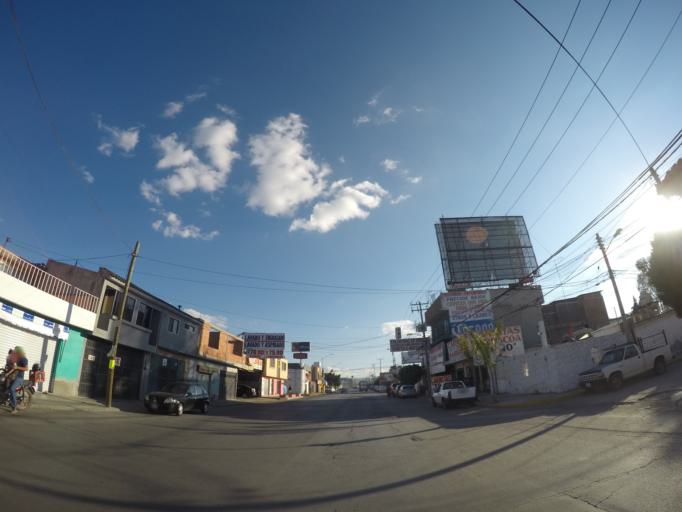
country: MX
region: San Luis Potosi
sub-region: San Luis Potosi
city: San Luis Potosi
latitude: 22.1777
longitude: -100.9964
